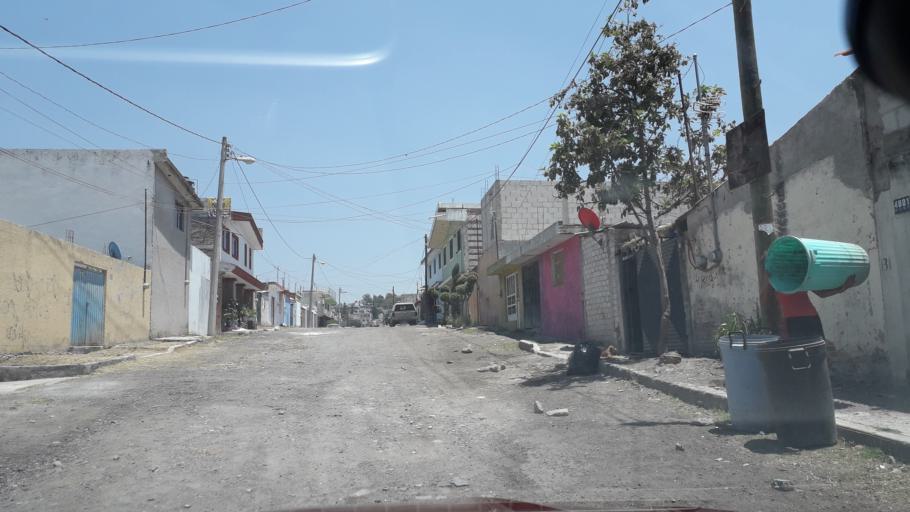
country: MX
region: Puebla
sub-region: Puebla
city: Galaxia la Calera
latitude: 18.9954
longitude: -98.1846
